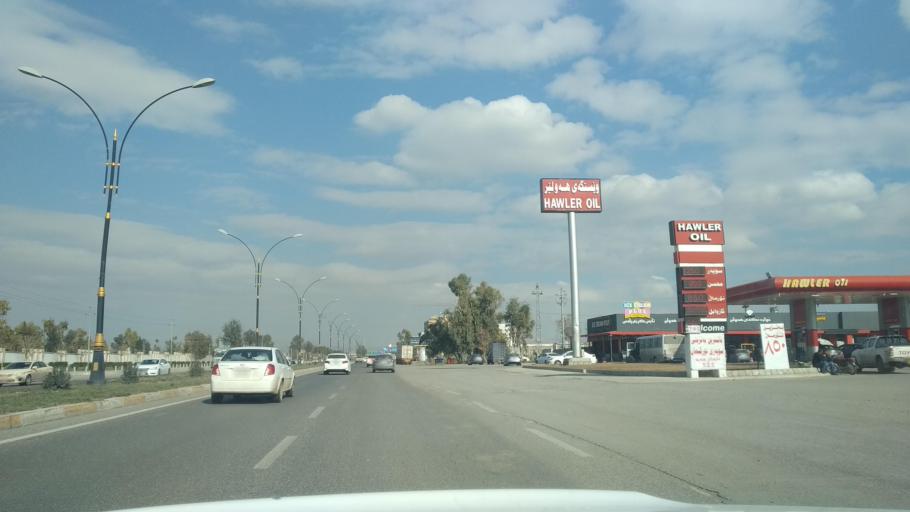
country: IQ
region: Arbil
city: Erbil
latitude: 36.2566
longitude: 44.0830
